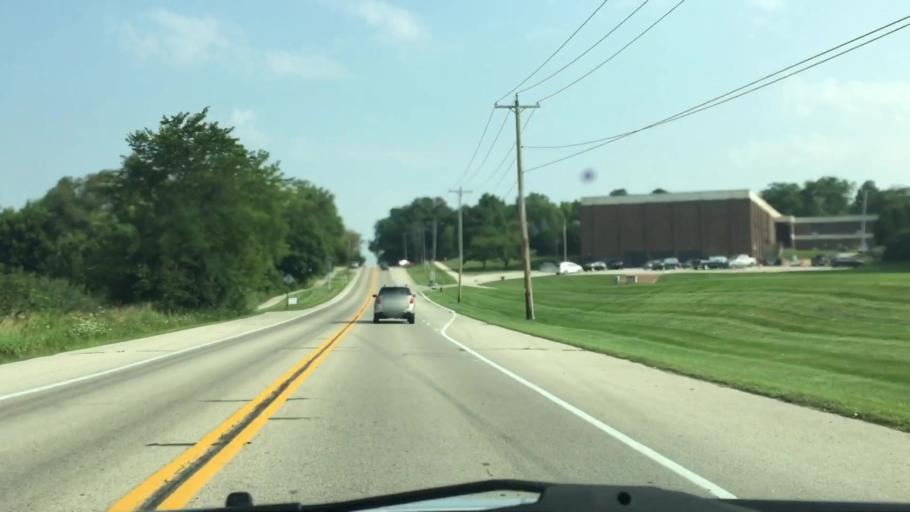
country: US
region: Wisconsin
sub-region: Waukesha County
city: Brookfield
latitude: 43.0802
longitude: -88.1459
